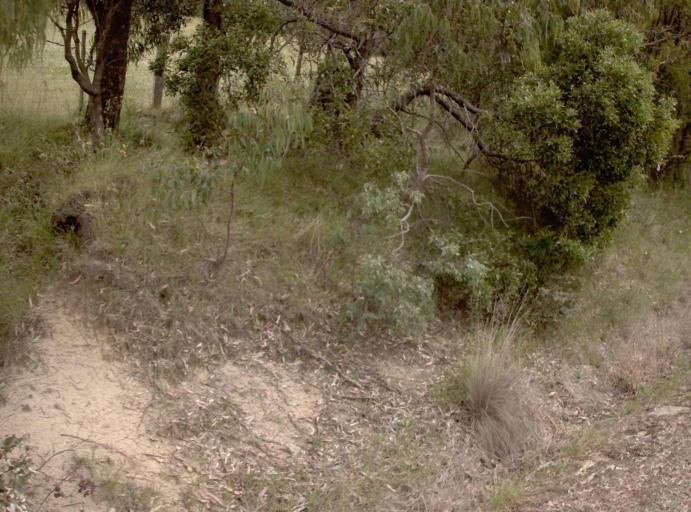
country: AU
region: Victoria
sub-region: East Gippsland
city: Bairnsdale
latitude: -37.5754
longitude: 147.1847
